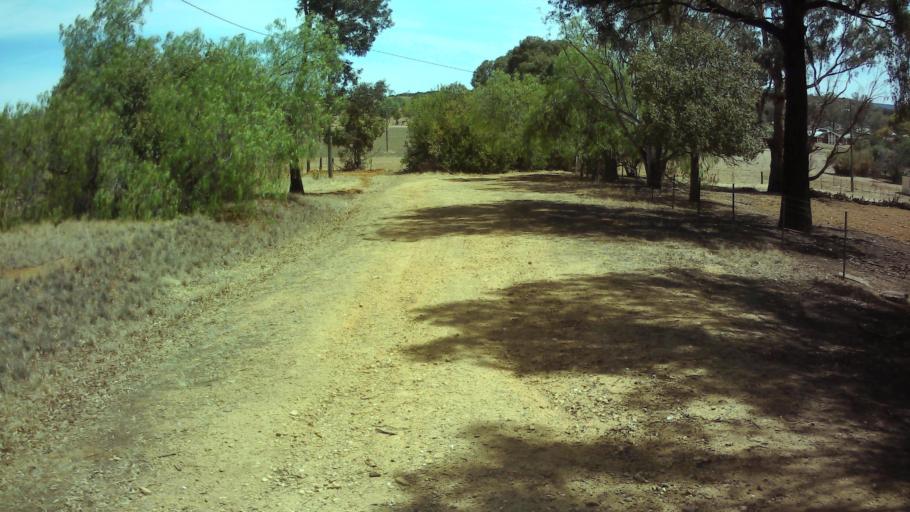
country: AU
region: New South Wales
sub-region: Weddin
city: Grenfell
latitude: -33.9028
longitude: 148.1662
